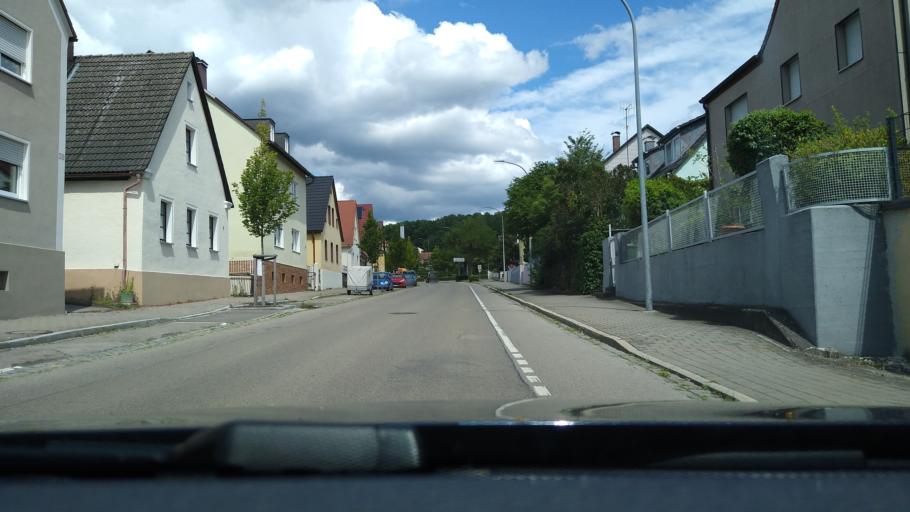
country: DE
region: Bavaria
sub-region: Regierungsbezirk Mittelfranken
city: Gunzenhausen
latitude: 49.1140
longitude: 10.7603
